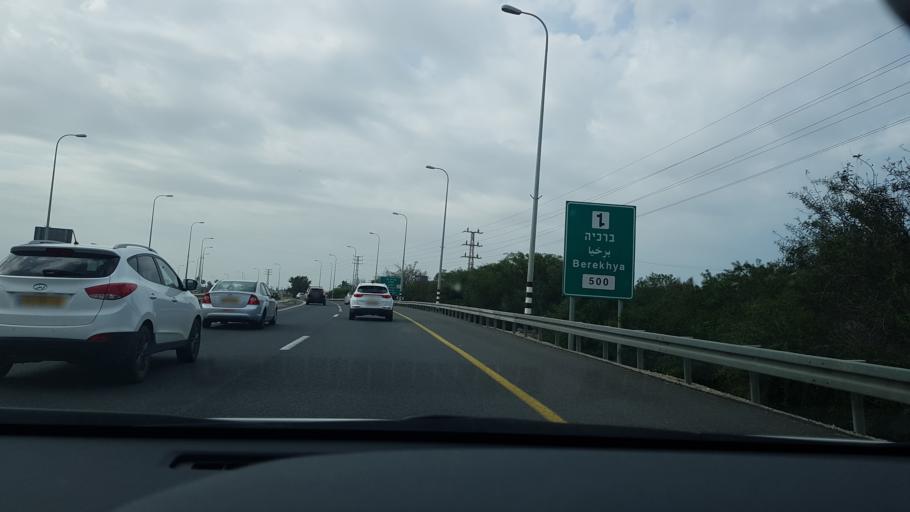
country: IL
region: Southern District
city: Ashqelon
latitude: 31.6717
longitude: 34.6075
